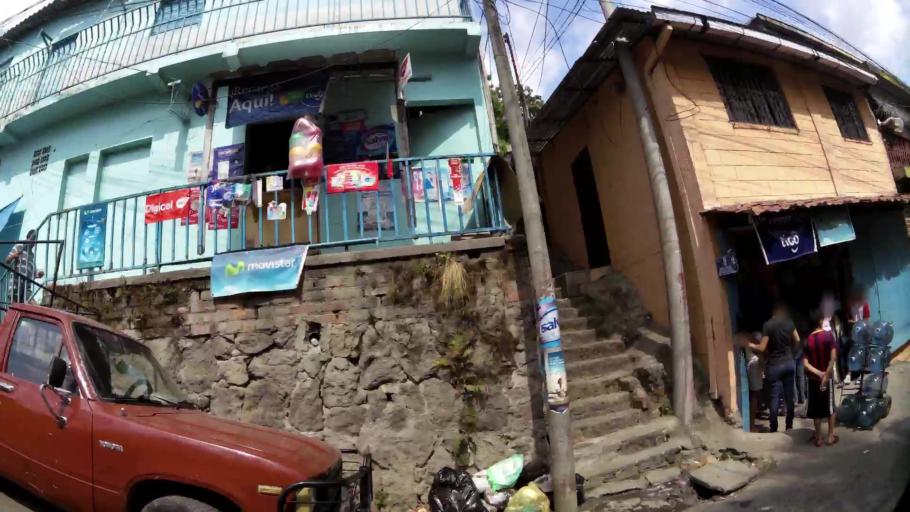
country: SV
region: San Salvador
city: Mejicanos
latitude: 13.7164
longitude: -89.2314
